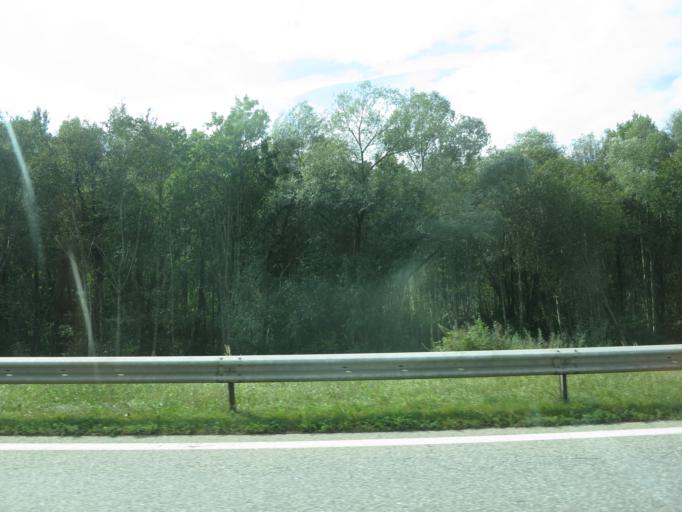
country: CH
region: Grisons
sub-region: Imboden District
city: Bonaduz
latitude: 46.8137
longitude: 9.4079
